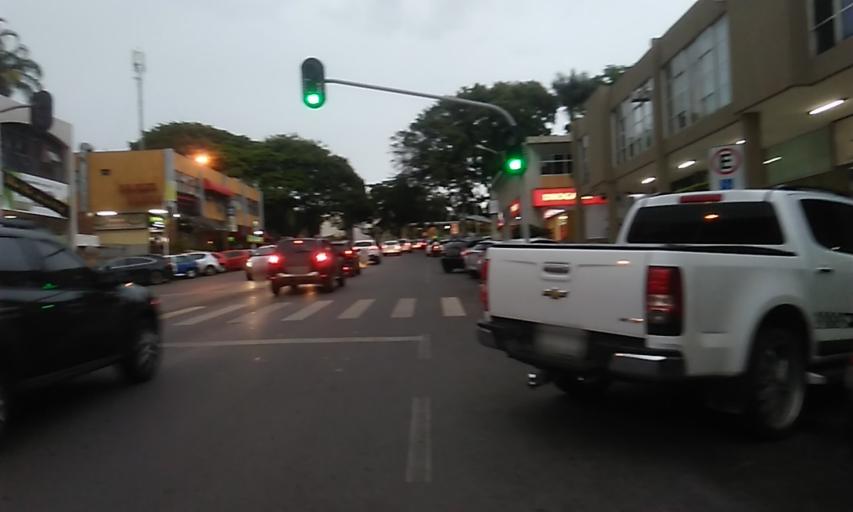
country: BR
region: Federal District
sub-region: Brasilia
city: Brasilia
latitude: -15.7773
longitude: -47.8833
